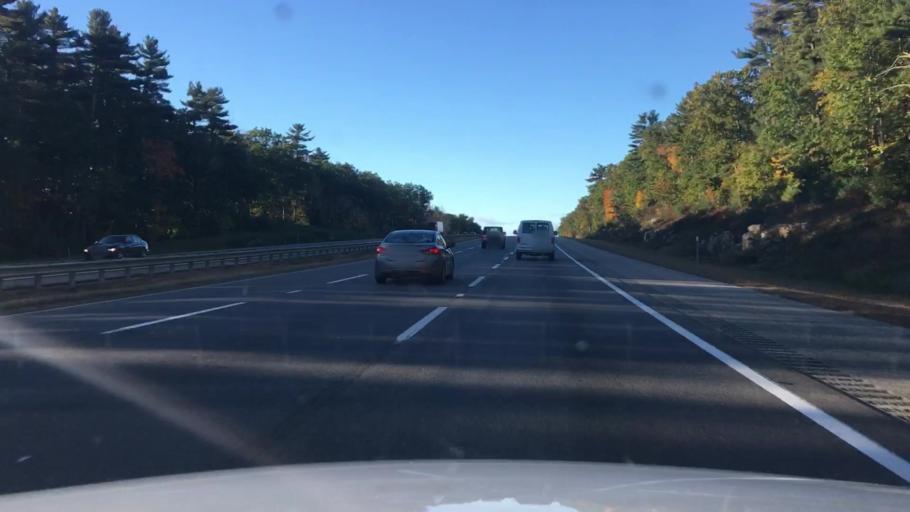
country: US
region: Maine
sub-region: York County
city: West Kennebunk
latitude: 43.3689
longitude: -70.5829
